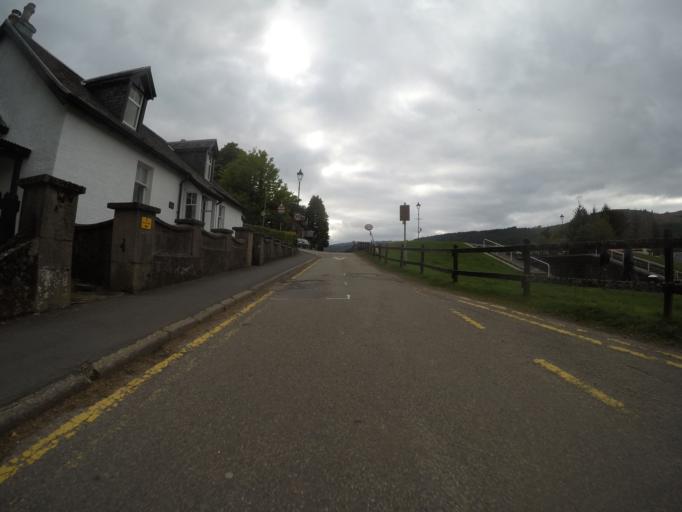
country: GB
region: Scotland
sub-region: Highland
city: Spean Bridge
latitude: 57.1445
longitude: -4.6839
